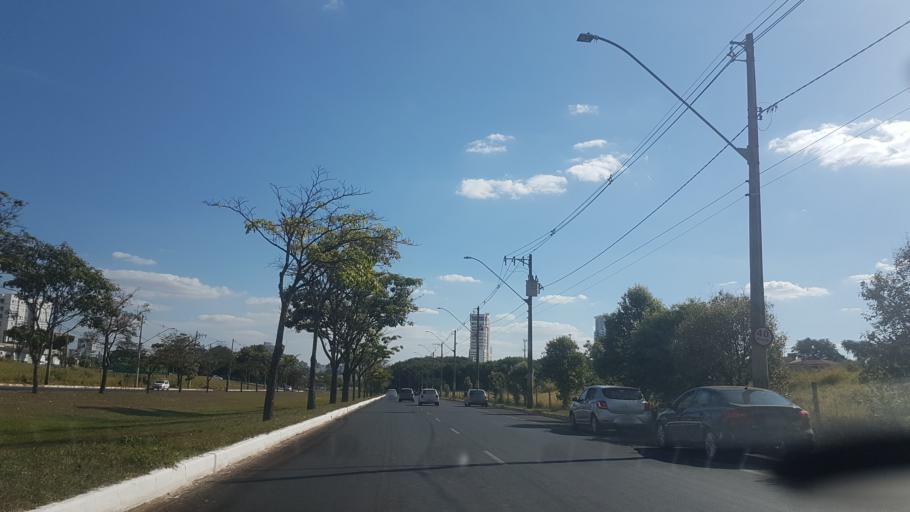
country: BR
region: Minas Gerais
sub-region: Uberlandia
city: Uberlandia
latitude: -18.9102
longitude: -48.2514
